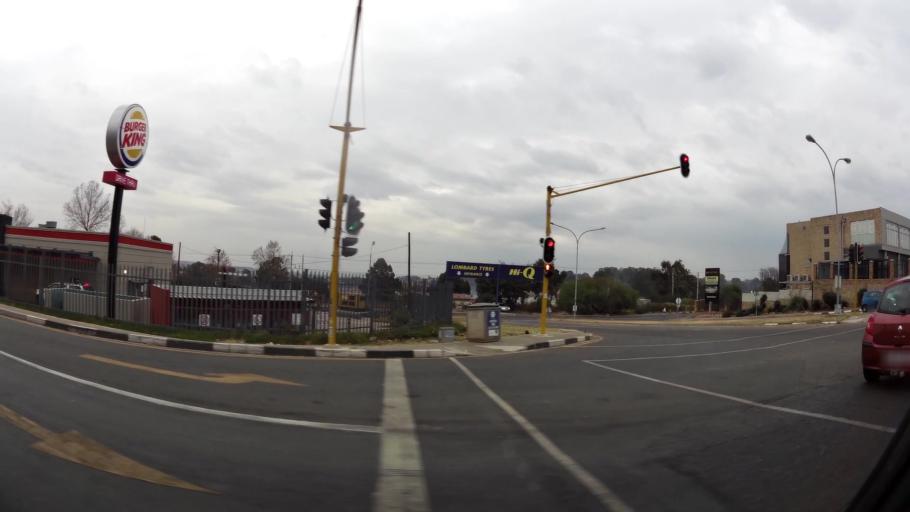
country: ZA
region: Gauteng
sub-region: City of Johannesburg Metropolitan Municipality
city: Roodepoort
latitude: -26.1329
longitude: 27.8562
